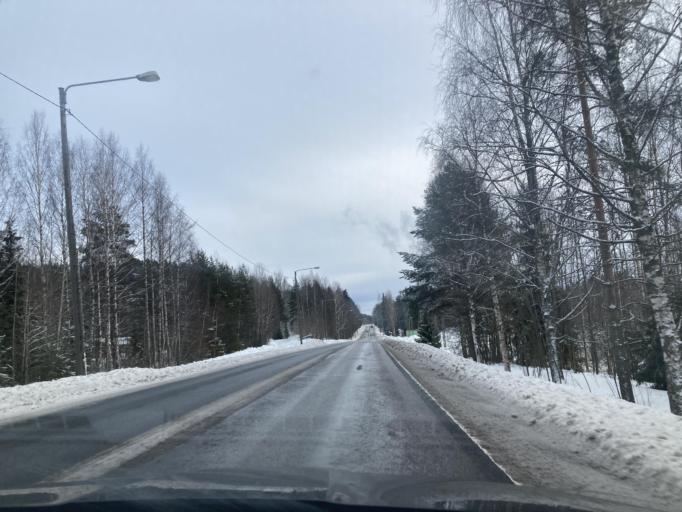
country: FI
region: Paijanne Tavastia
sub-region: Lahti
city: Asikkala
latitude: 61.1820
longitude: 25.4953
